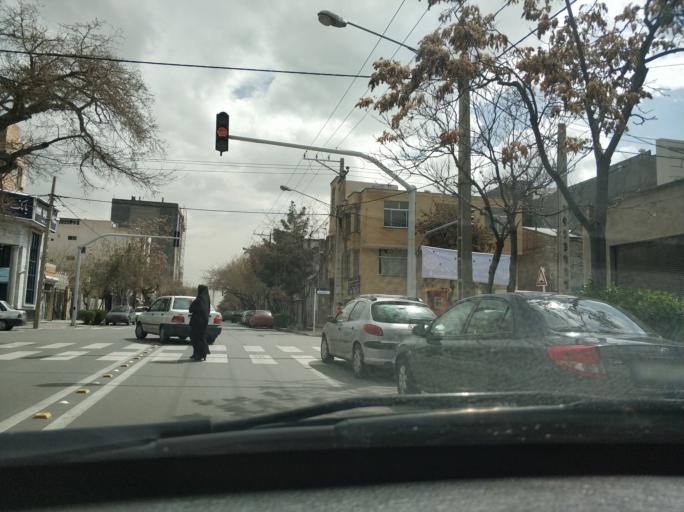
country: IR
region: Razavi Khorasan
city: Mashhad
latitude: 36.2806
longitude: 59.5735
